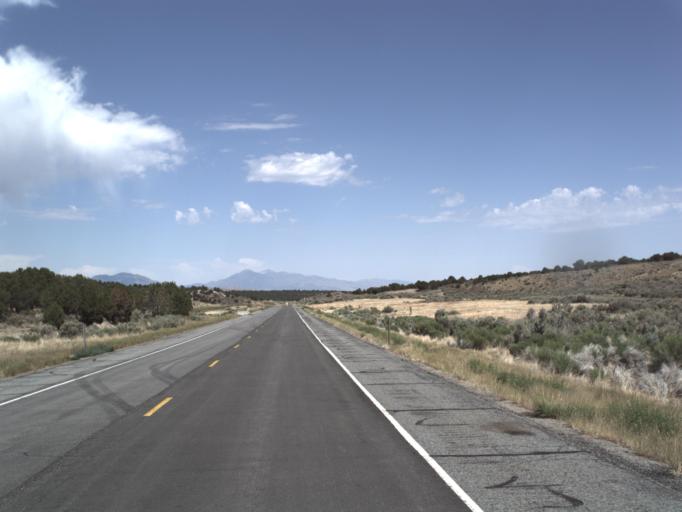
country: US
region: Utah
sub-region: Utah County
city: Eagle Mountain
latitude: 39.9843
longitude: -112.2628
